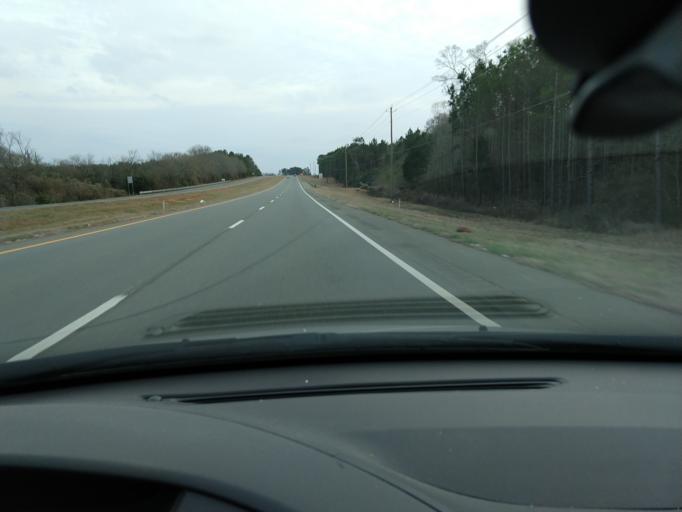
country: US
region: Georgia
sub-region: Sumter County
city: Americus
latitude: 32.0533
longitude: -84.2541
